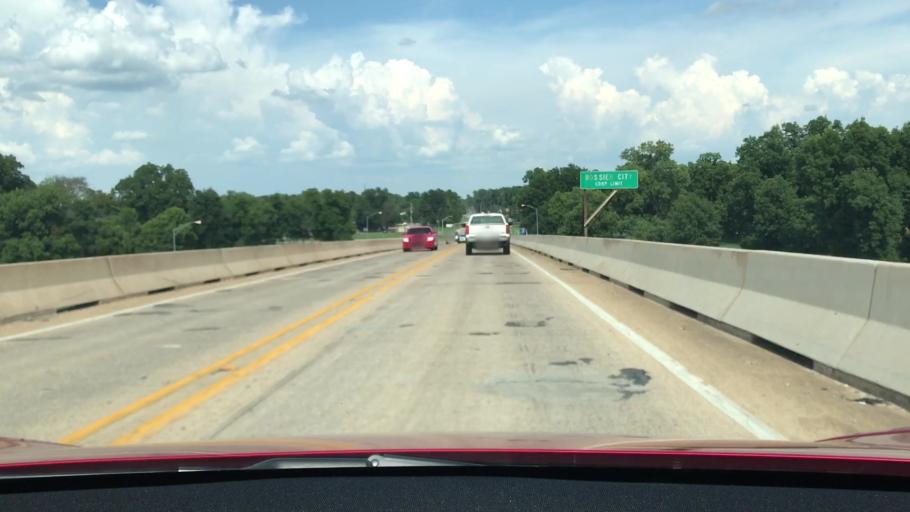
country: US
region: Louisiana
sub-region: Bossier Parish
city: Bossier City
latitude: 32.4588
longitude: -93.6760
